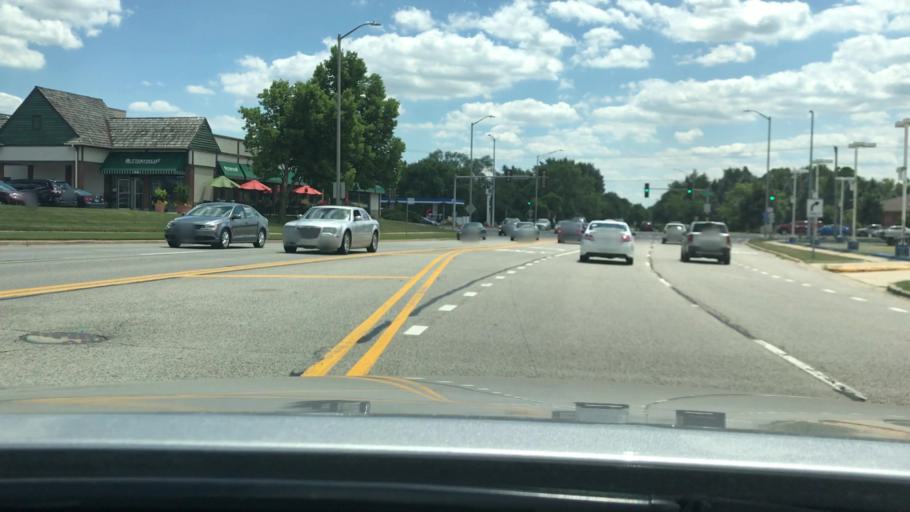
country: US
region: Illinois
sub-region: DuPage County
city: Naperville
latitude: 41.7970
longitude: -88.1192
